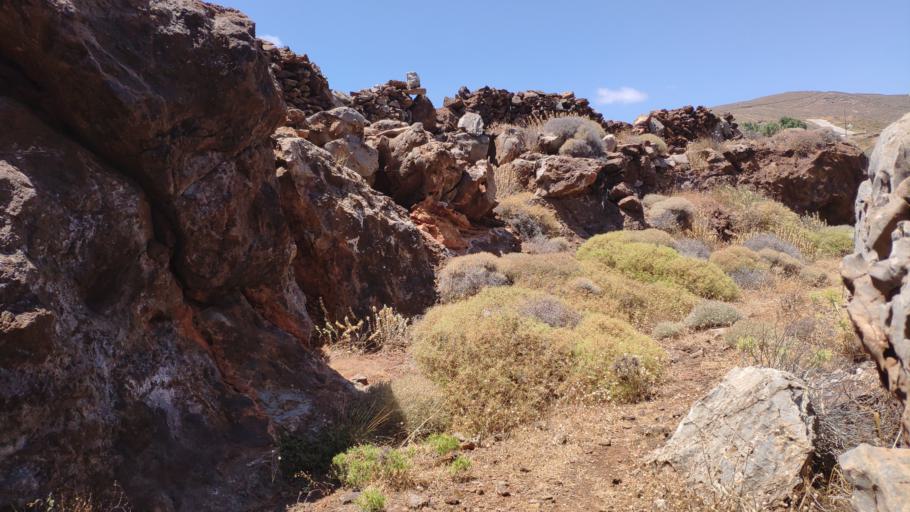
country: GR
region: South Aegean
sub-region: Nomos Kykladon
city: Kythnos
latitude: 37.3795
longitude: 24.4553
